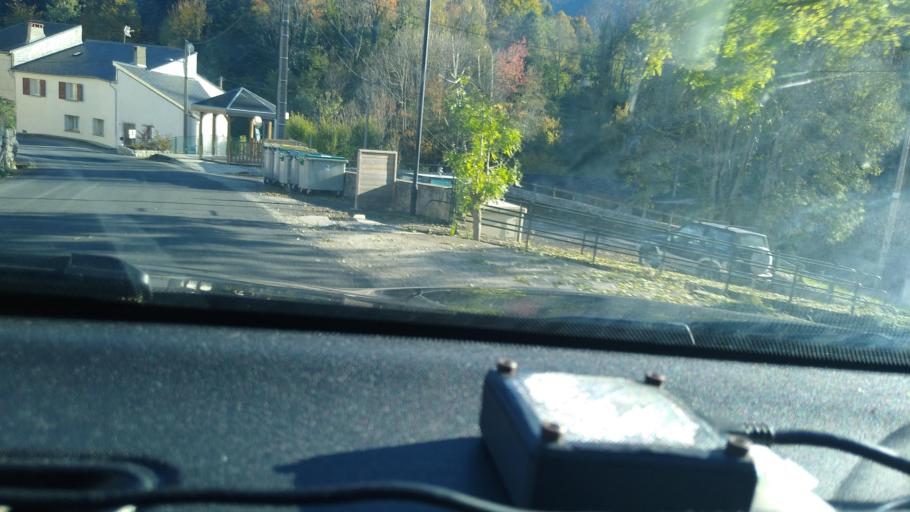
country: FR
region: Languedoc-Roussillon
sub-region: Departement de l'Aude
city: Quillan
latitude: 42.7374
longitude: 2.2000
